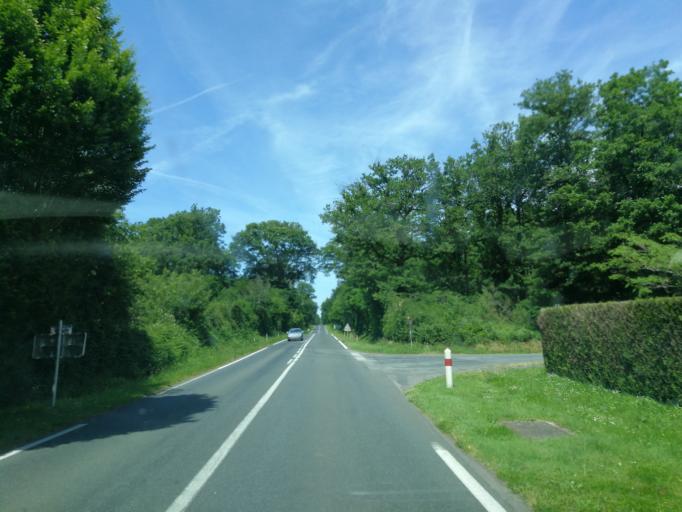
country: FR
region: Pays de la Loire
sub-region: Departement de la Vendee
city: Pissotte
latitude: 46.5341
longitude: -0.8073
